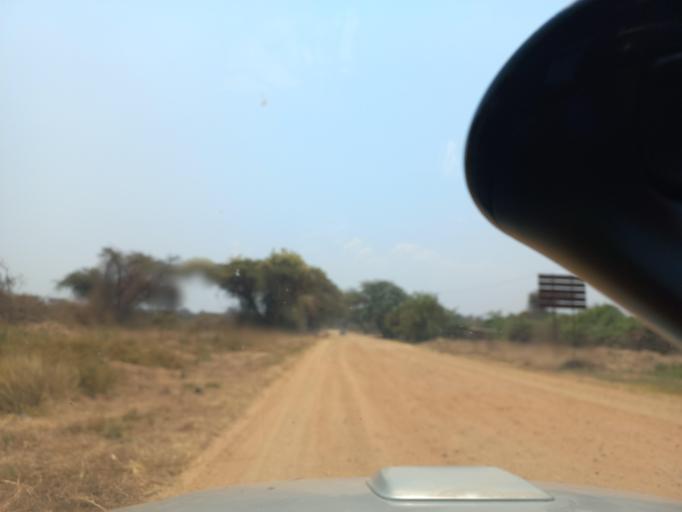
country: ZW
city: Chirundu
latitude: -15.9368
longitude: 28.8724
